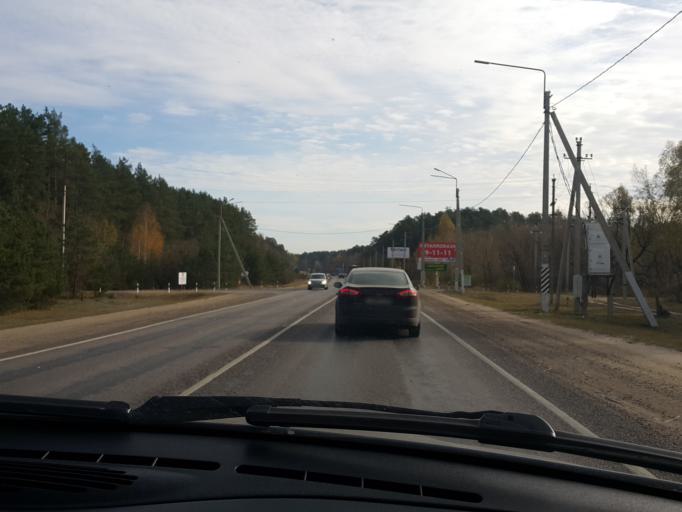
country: RU
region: Tambov
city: Donskoye
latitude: 52.7111
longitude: 41.5259
